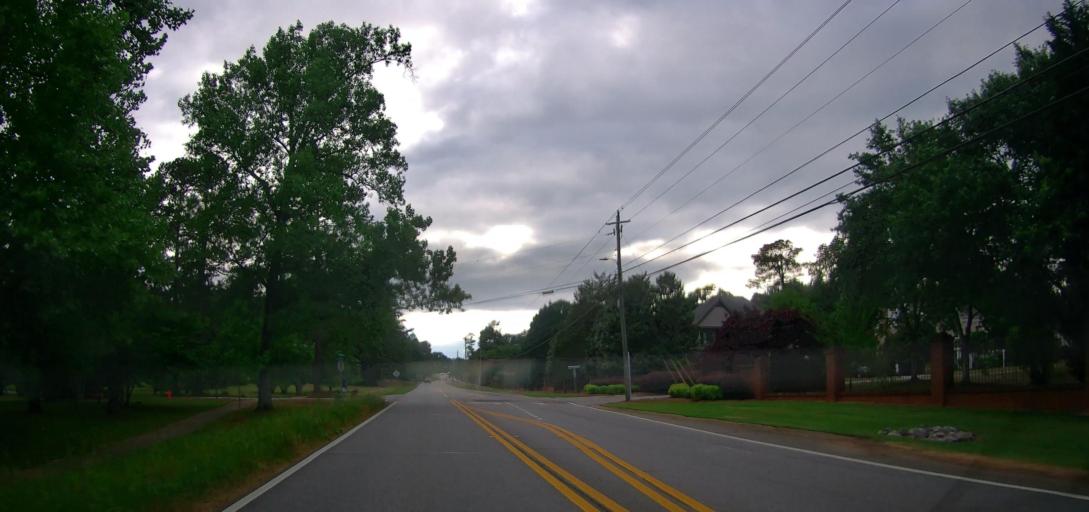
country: US
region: Georgia
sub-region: Clarke County
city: Country Club Estates
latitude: 33.9343
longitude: -83.4305
